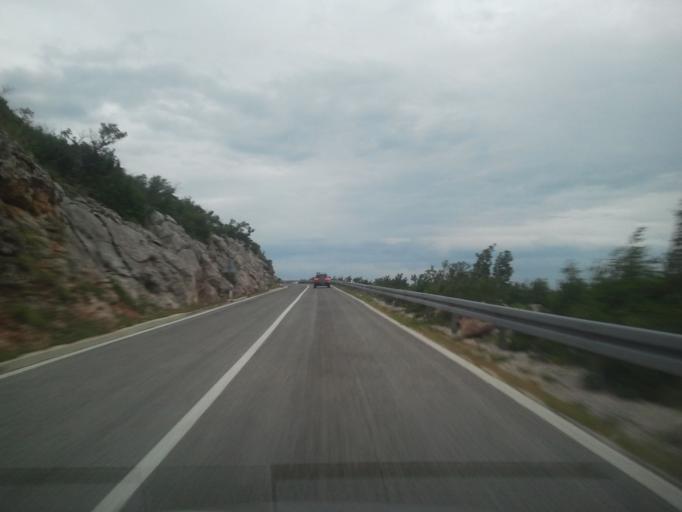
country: HR
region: Zadarska
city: Gracac
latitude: 44.2266
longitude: 15.7875
